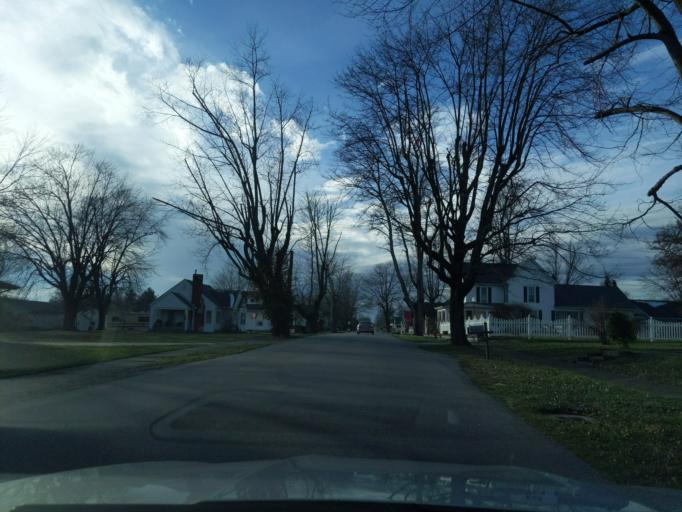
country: US
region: Indiana
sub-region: Decatur County
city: Westport
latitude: 39.1758
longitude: -85.5781
